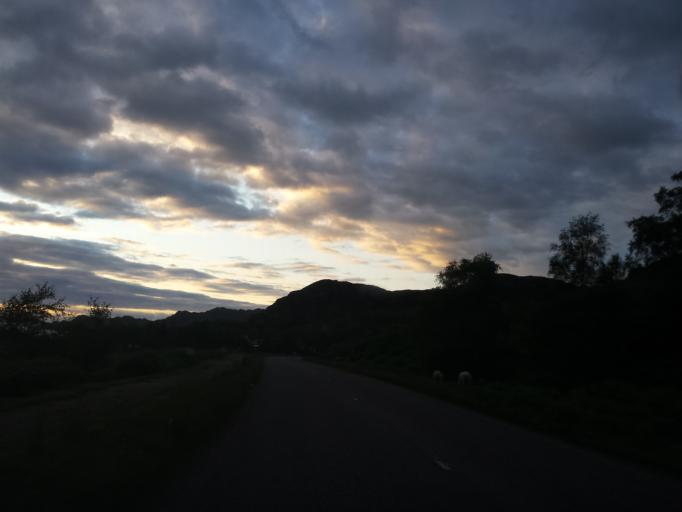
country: GB
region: Scotland
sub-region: Highland
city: Portree
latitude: 57.5220
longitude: -5.6454
